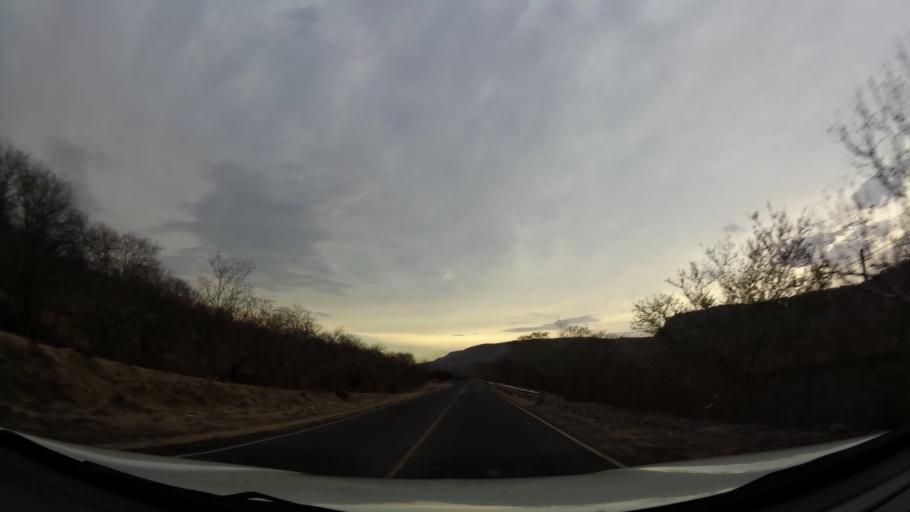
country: NI
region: Leon
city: La Jicaral
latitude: 12.6829
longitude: -86.4222
